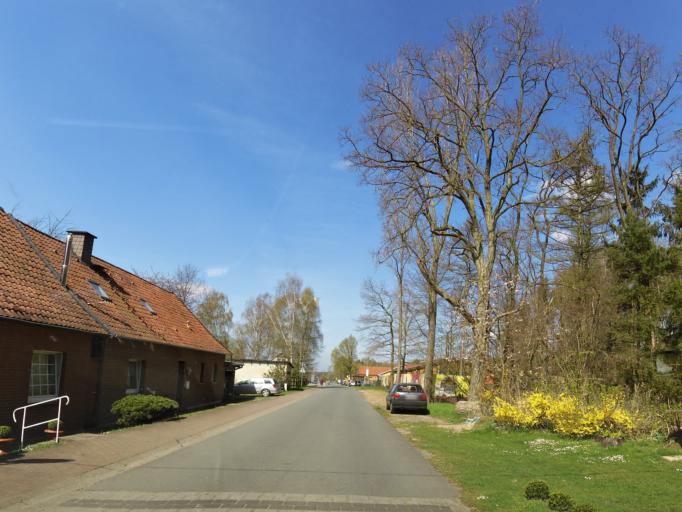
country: DE
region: Lower Saxony
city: Rehburg-Loccum
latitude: 52.4409
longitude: 9.2013
